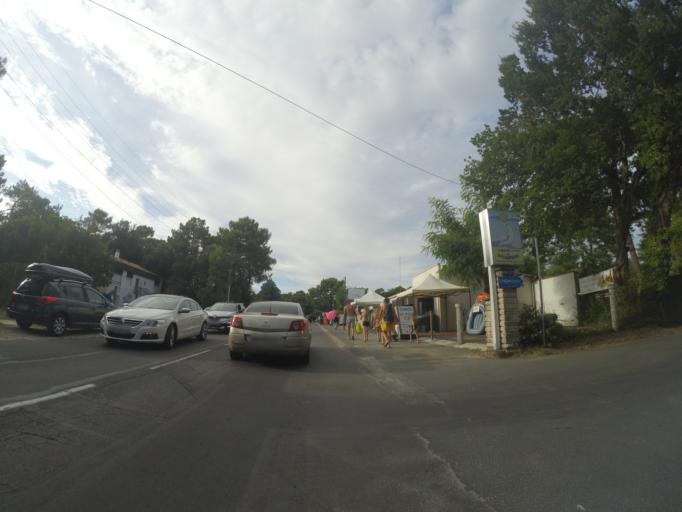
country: FR
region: Poitou-Charentes
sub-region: Departement de la Charente-Maritime
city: Saint-Georges-de-Didonne
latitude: 45.5844
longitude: -0.9855
